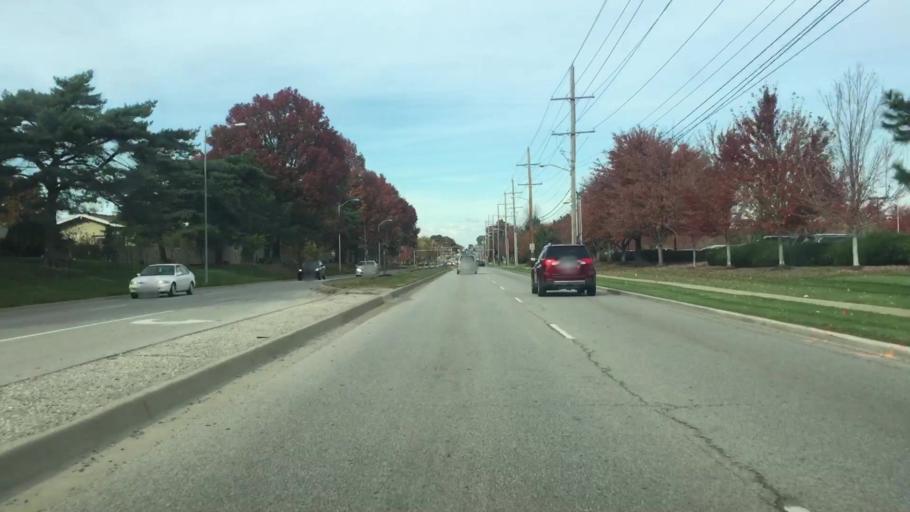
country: US
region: Kansas
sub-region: Johnson County
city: Lenexa
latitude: 38.9824
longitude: -94.7236
